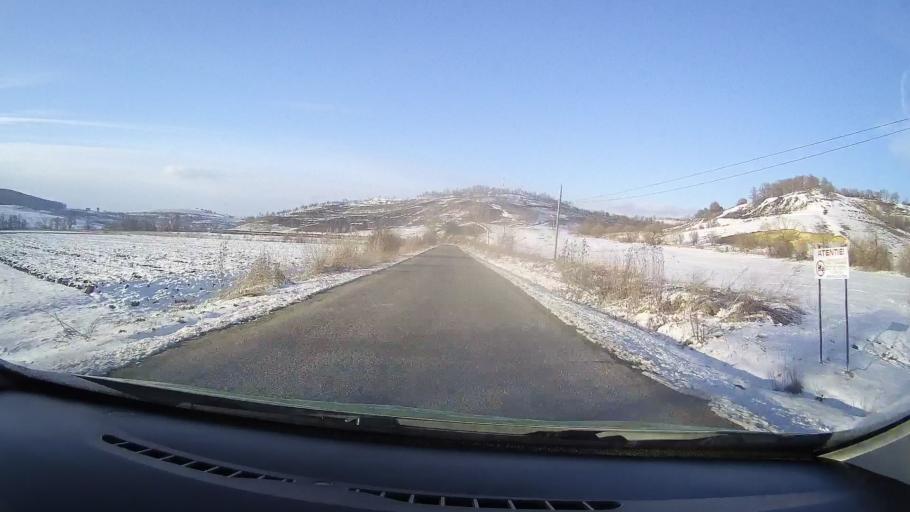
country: RO
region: Sibiu
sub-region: Comuna Merghindeal
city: Merghindeal
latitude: 45.9725
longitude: 24.7073
